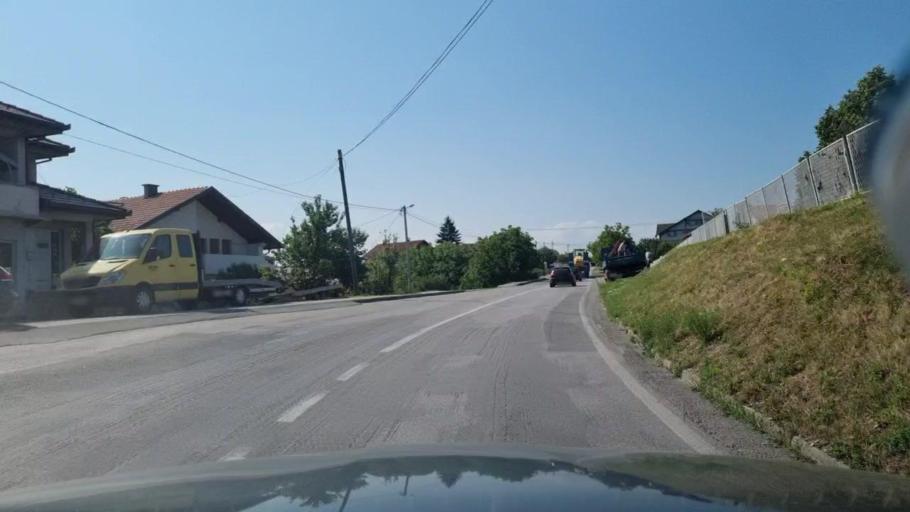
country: BA
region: Federation of Bosnia and Herzegovina
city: Gradacac
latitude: 44.8699
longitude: 18.4313
